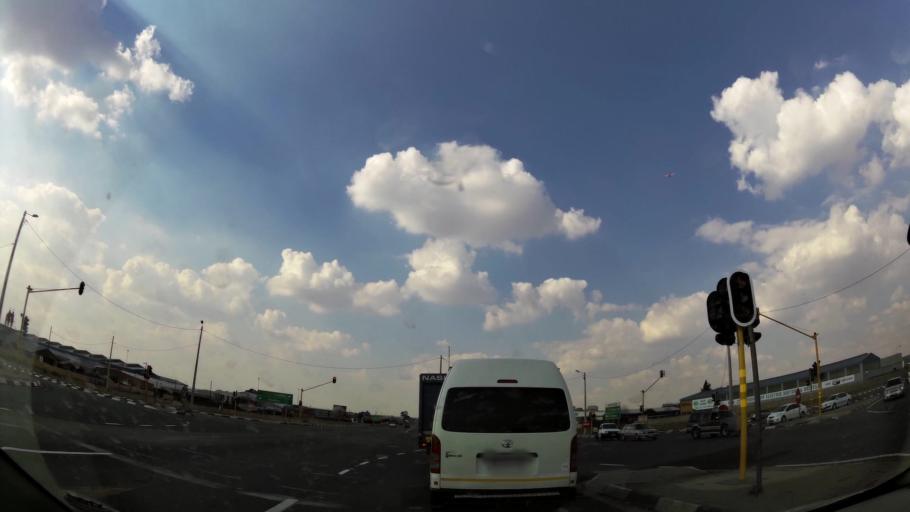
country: ZA
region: Gauteng
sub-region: Ekurhuleni Metropolitan Municipality
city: Germiston
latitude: -26.3012
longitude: 28.1892
